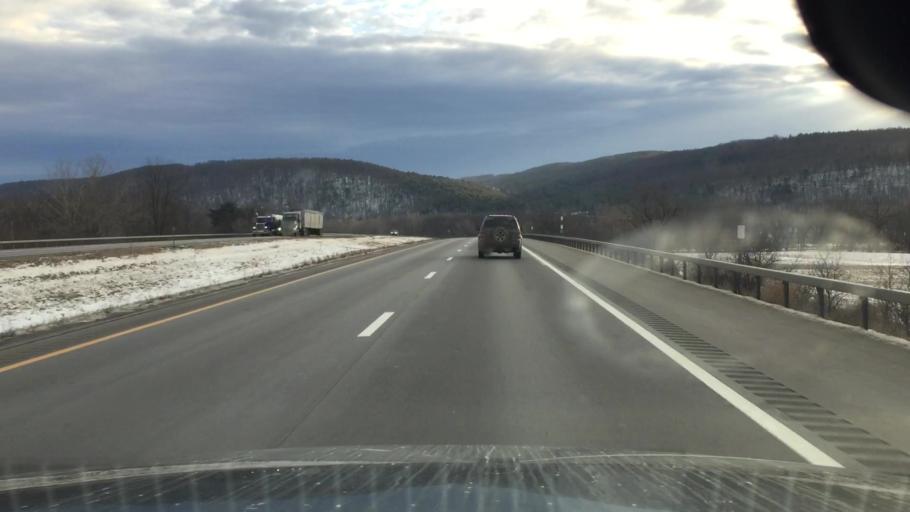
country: US
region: Pennsylvania
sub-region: Bradford County
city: Sayre
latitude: 42.0068
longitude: -76.4756
